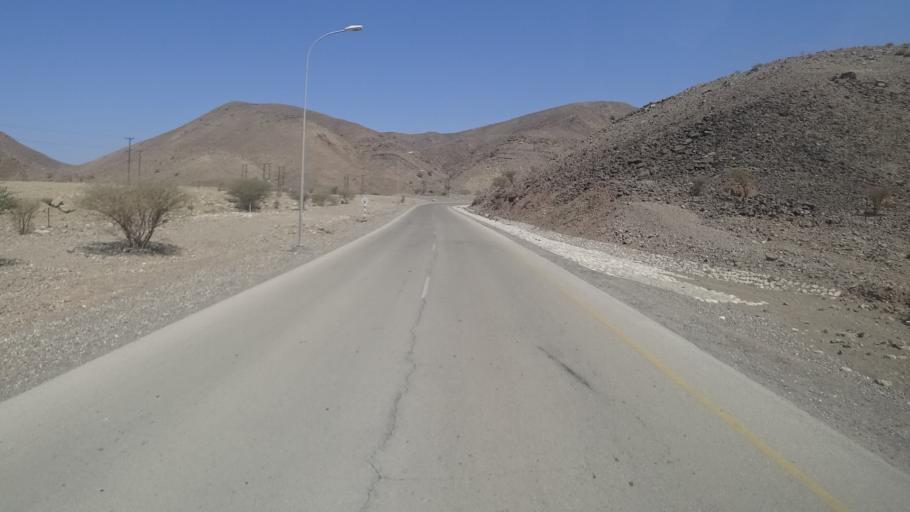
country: OM
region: Ash Sharqiyah
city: Badiyah
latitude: 22.5301
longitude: 58.9555
